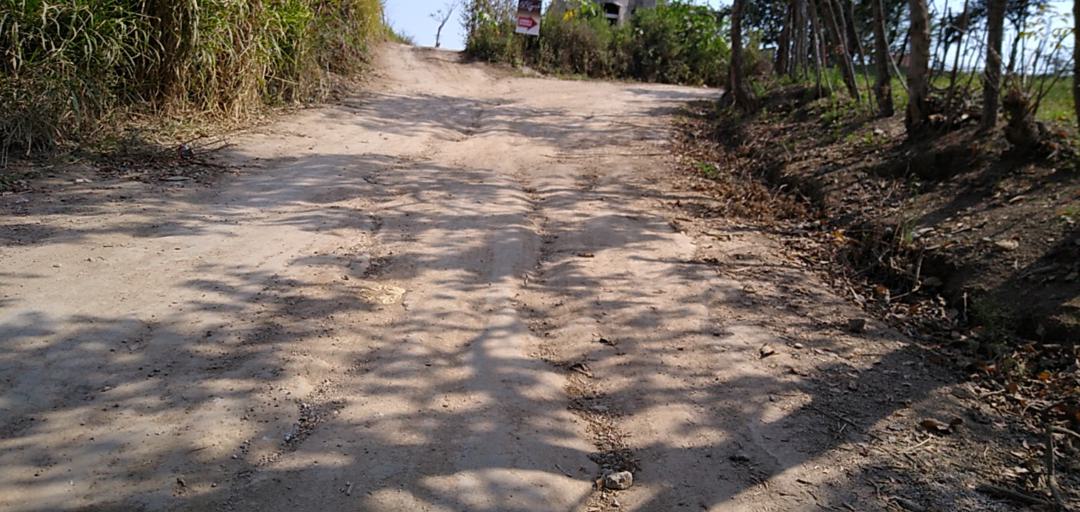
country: MX
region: Nayarit
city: Tepic
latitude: 21.5337
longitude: -104.9111
